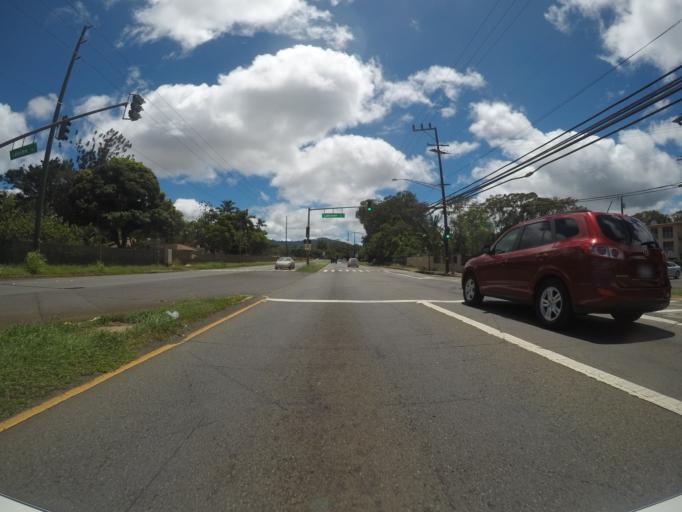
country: US
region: Hawaii
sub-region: Honolulu County
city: Wahiawa
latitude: 21.4895
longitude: -158.0352
